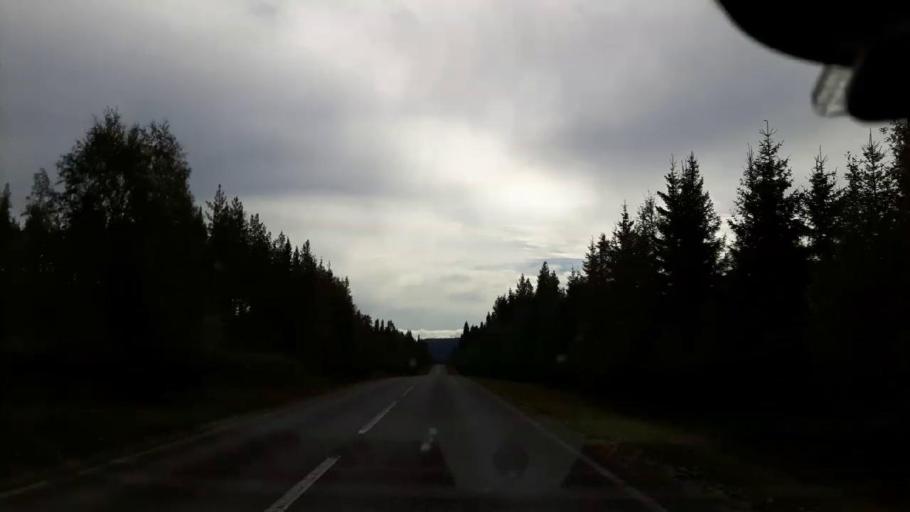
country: SE
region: Jaemtland
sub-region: Ragunda Kommun
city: Hammarstrand
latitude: 63.0582
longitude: 15.9271
